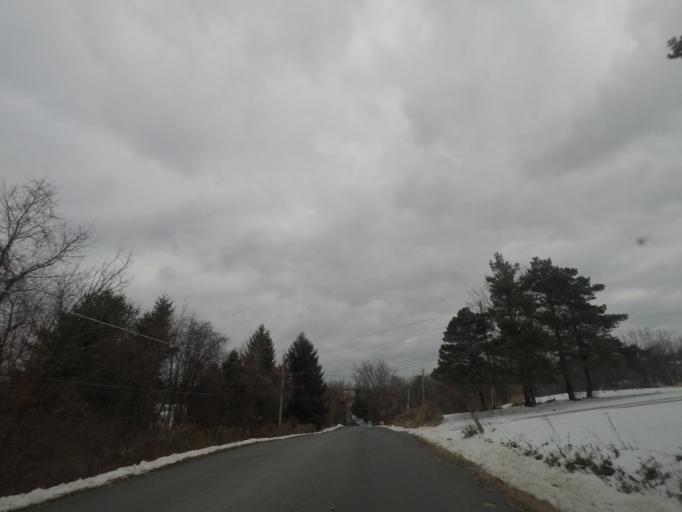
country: US
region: New York
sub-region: Rensselaer County
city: West Sand Lake
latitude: 42.5972
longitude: -73.6311
